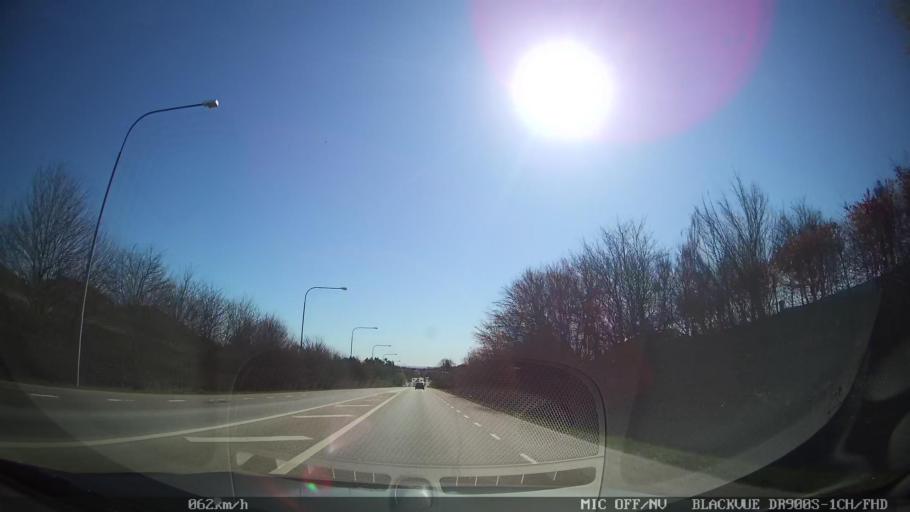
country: SE
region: Skane
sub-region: Ystads Kommun
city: Ystad
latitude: 55.4360
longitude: 13.7967
